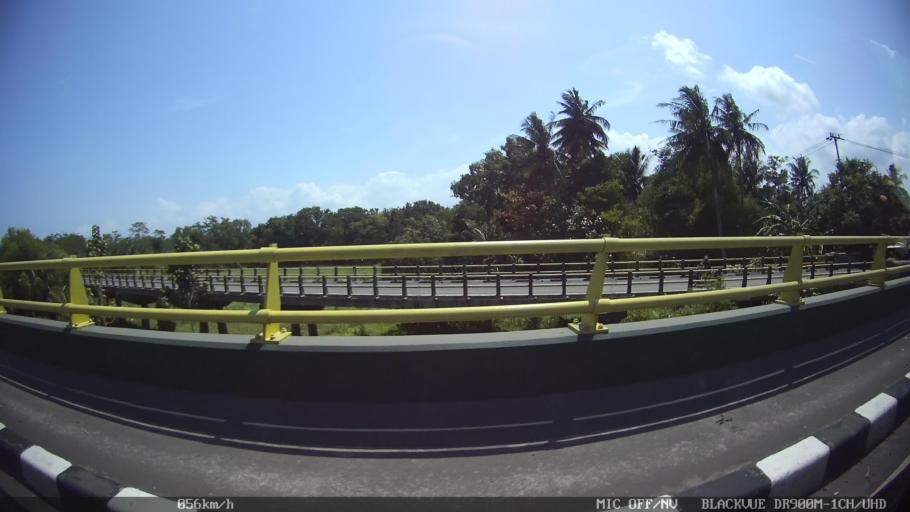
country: ID
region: Daerah Istimewa Yogyakarta
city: Srandakan
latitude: -7.9386
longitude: 110.2460
